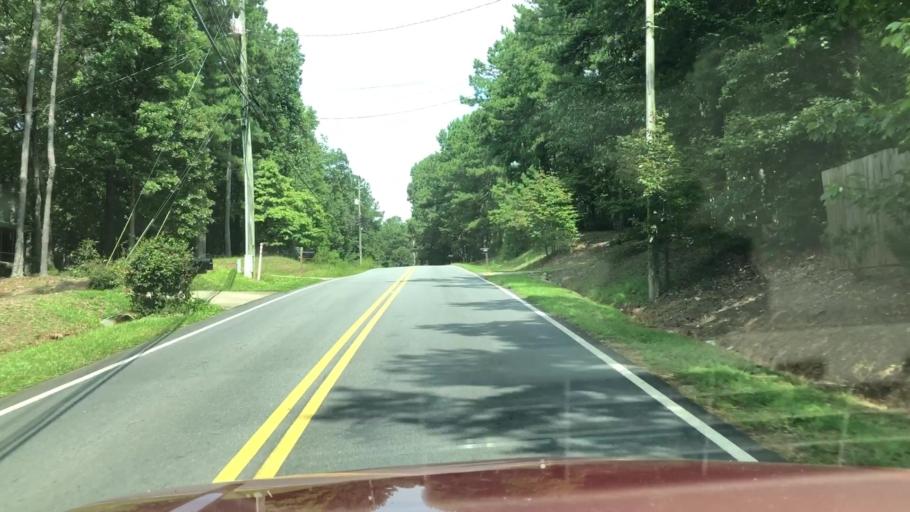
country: US
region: Georgia
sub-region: Cherokee County
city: Woodstock
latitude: 34.1512
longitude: -84.5946
